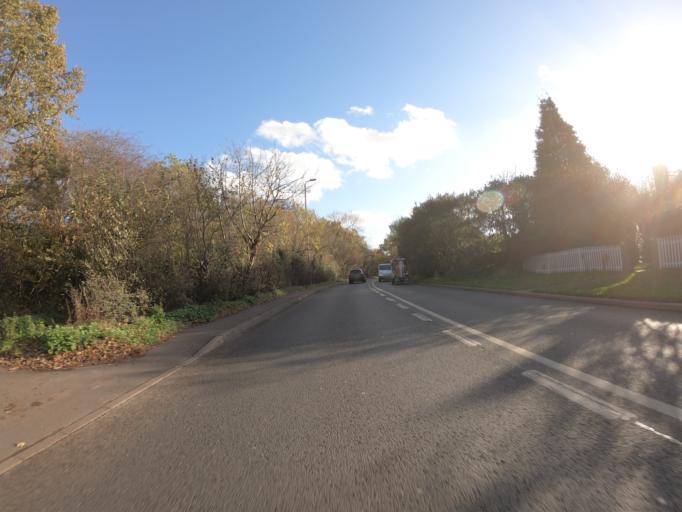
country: GB
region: England
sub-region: Greater London
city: Chislehurst
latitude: 51.4081
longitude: 0.0817
